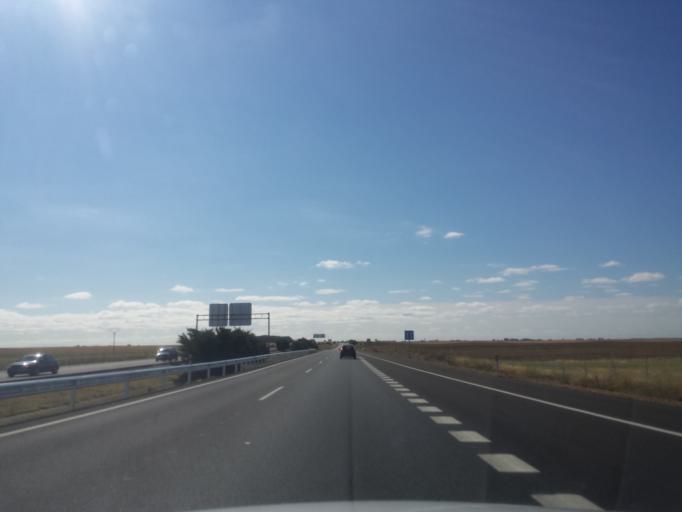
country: ES
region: Castille and Leon
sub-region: Provincia de Zamora
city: Castrogonzalo
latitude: 41.9629
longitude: -5.5868
